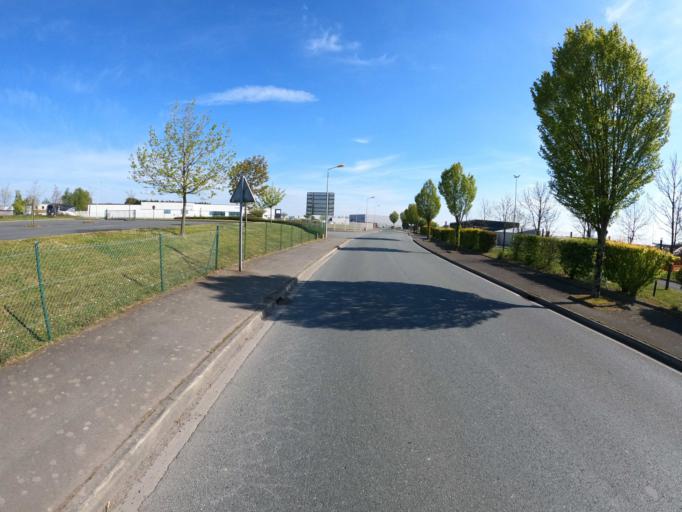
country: FR
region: Pays de la Loire
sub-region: Departement de Maine-et-Loire
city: La Seguiniere
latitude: 47.0738
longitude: -0.9392
